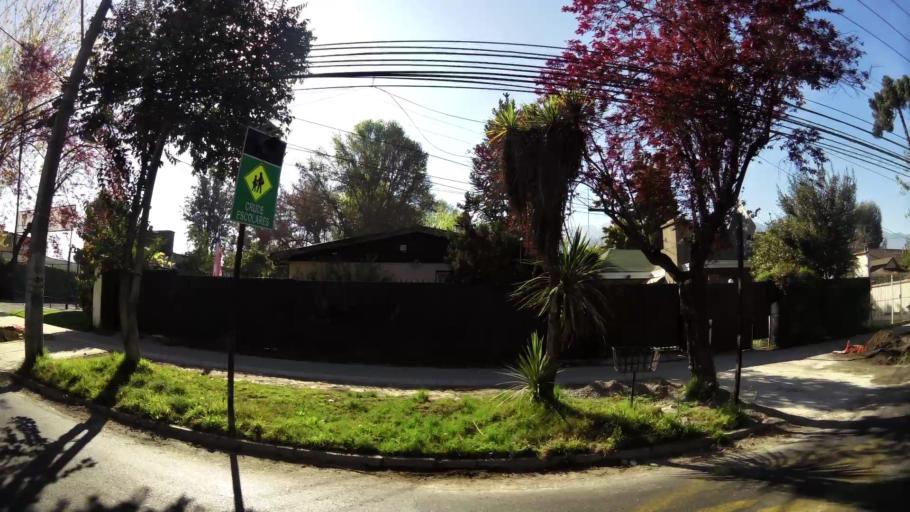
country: CL
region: Santiago Metropolitan
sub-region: Provincia de Santiago
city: Villa Presidente Frei, Nunoa, Santiago, Chile
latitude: -33.4333
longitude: -70.5547
